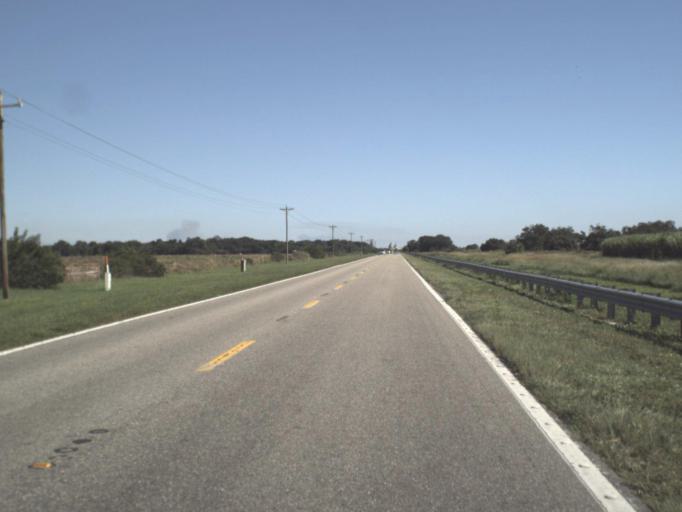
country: US
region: Florida
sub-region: Glades County
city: Moore Haven
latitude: 26.7578
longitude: -81.1551
